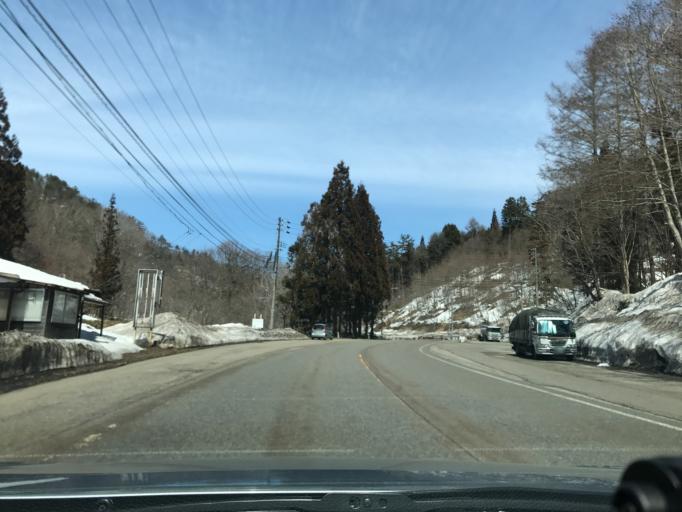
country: JP
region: Nagano
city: Omachi
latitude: 36.5842
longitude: 137.8408
